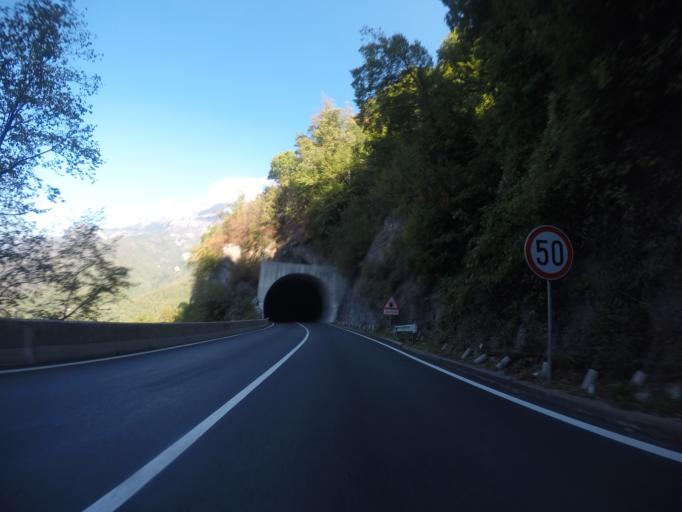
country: ME
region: Opstina Kolasin
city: Kolasin
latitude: 42.8083
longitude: 19.3952
